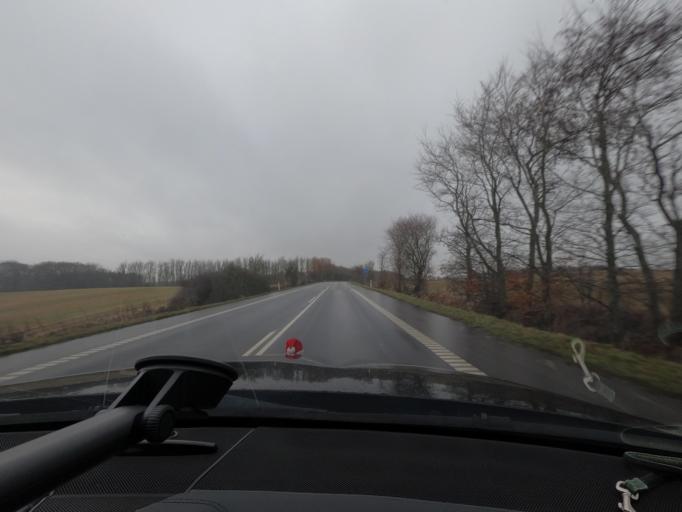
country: DK
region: South Denmark
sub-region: Sonderborg Kommune
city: Horuphav
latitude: 54.9095
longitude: 9.9207
